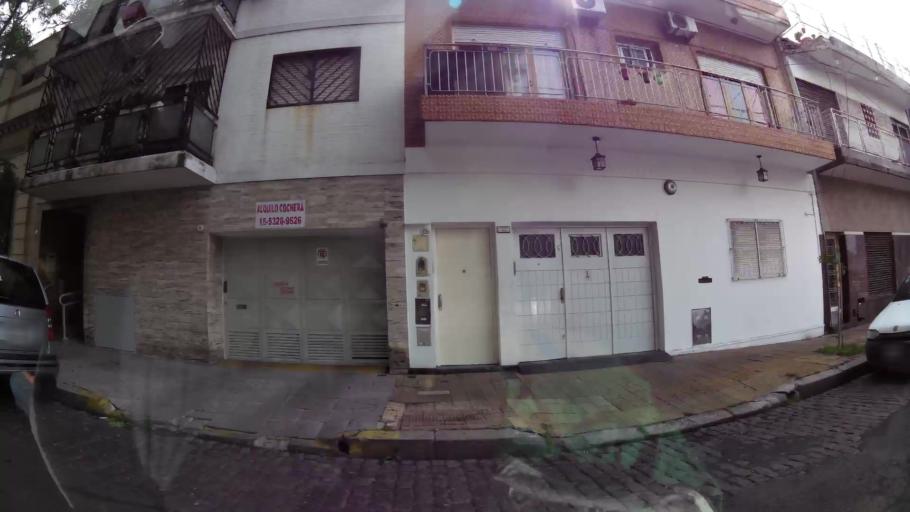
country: AR
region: Buenos Aires F.D.
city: Villa Santa Rita
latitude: -34.6357
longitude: -58.4953
